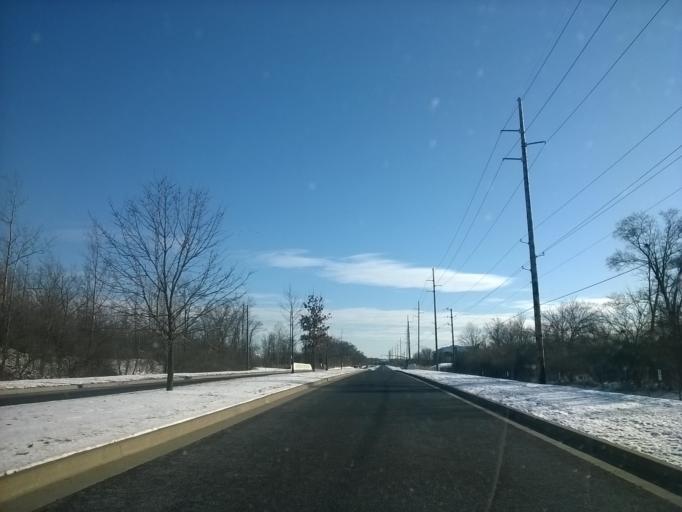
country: US
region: Indiana
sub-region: Hamilton County
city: Carmel
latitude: 39.9370
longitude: -86.0888
